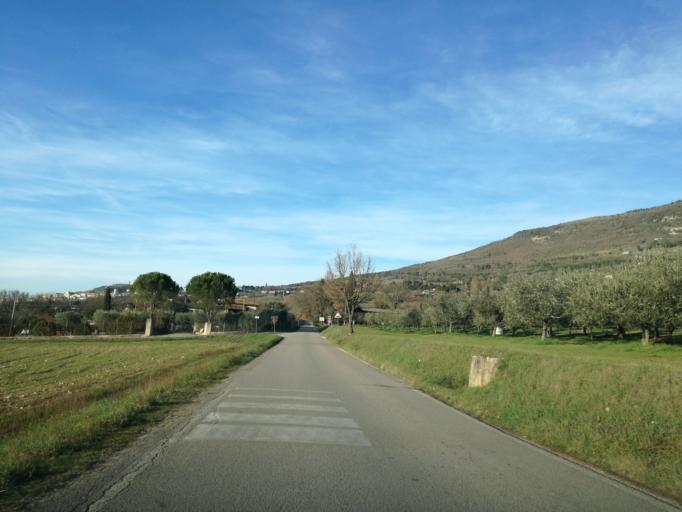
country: IT
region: Umbria
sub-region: Provincia di Perugia
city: Rivotorto
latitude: 43.0479
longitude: 12.6271
